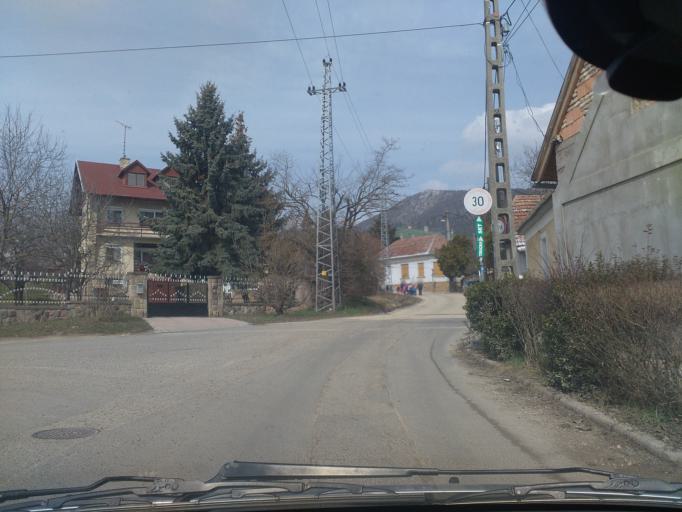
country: HU
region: Pest
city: Pilisborosjeno
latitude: 47.6093
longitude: 18.9898
